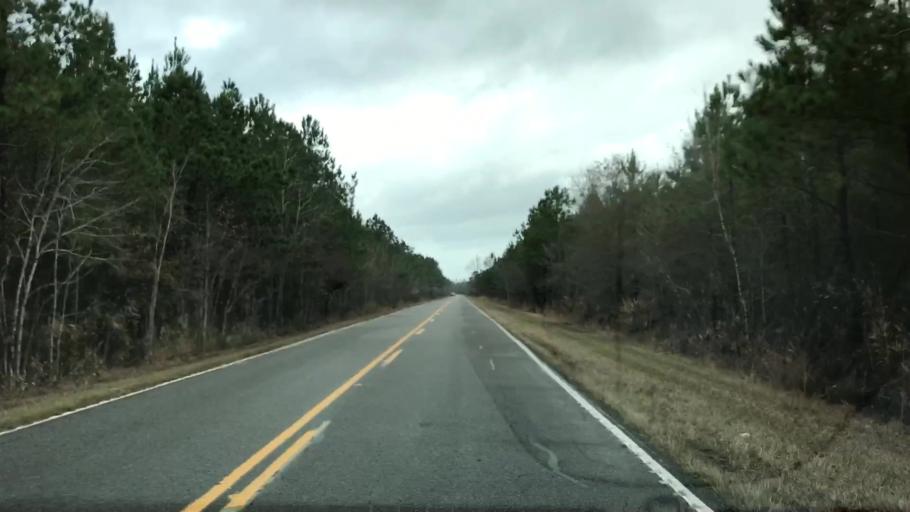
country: US
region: South Carolina
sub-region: Georgetown County
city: Murrells Inlet
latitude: 33.6258
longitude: -79.2404
